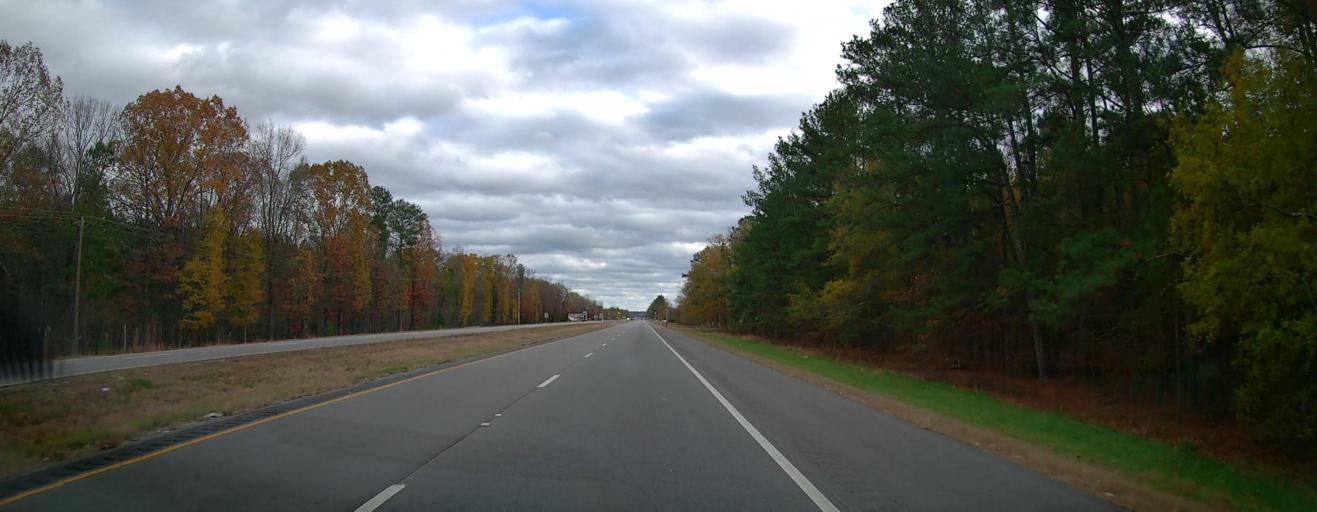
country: US
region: Alabama
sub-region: Lawrence County
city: Town Creek
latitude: 34.6568
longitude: -87.5353
